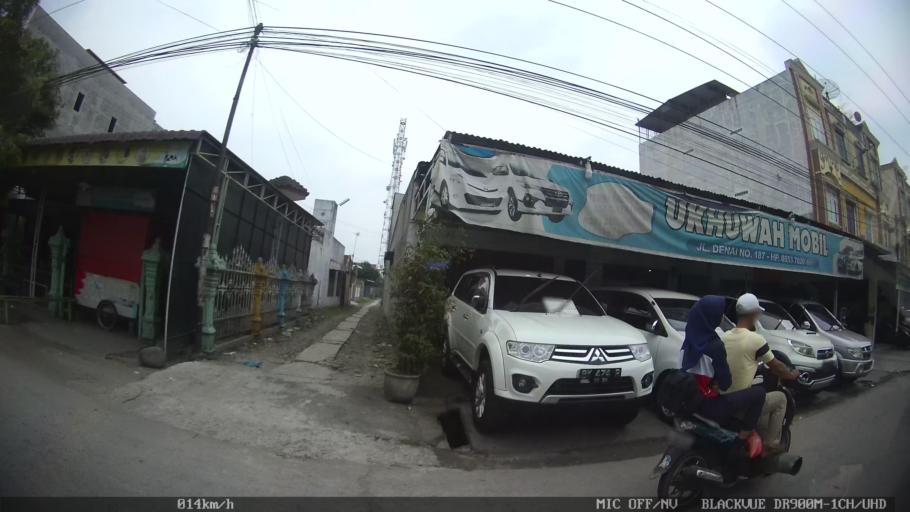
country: ID
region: North Sumatra
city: Medan
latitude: 3.5820
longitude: 98.7190
